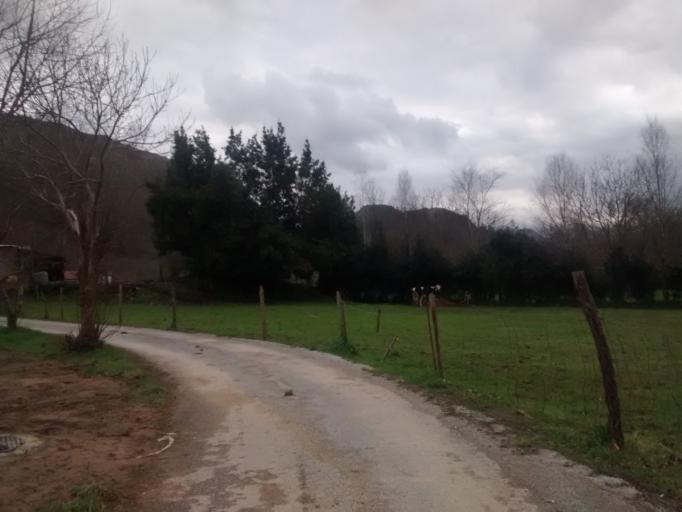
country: ES
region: Cantabria
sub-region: Provincia de Cantabria
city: Entrambasaguas
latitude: 43.3430
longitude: -3.6823
